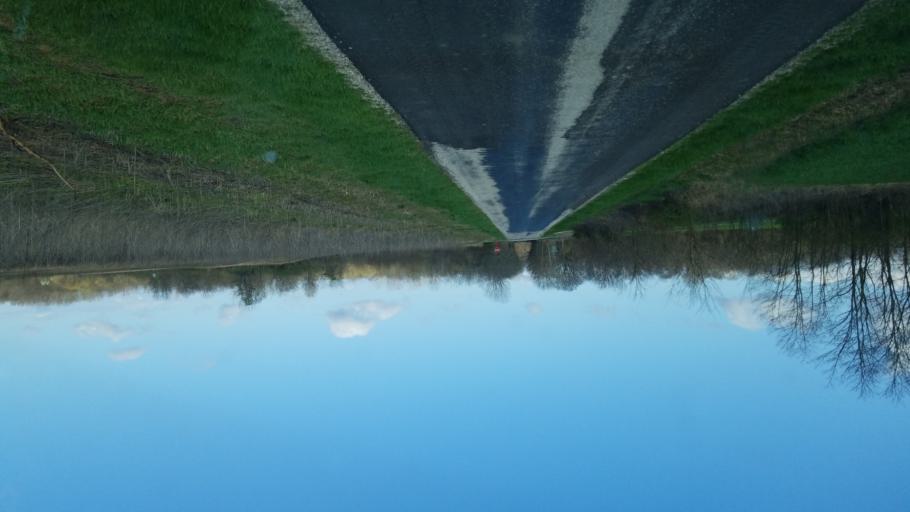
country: US
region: Ohio
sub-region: Delaware County
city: Ashley
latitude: 40.3907
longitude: -83.0362
